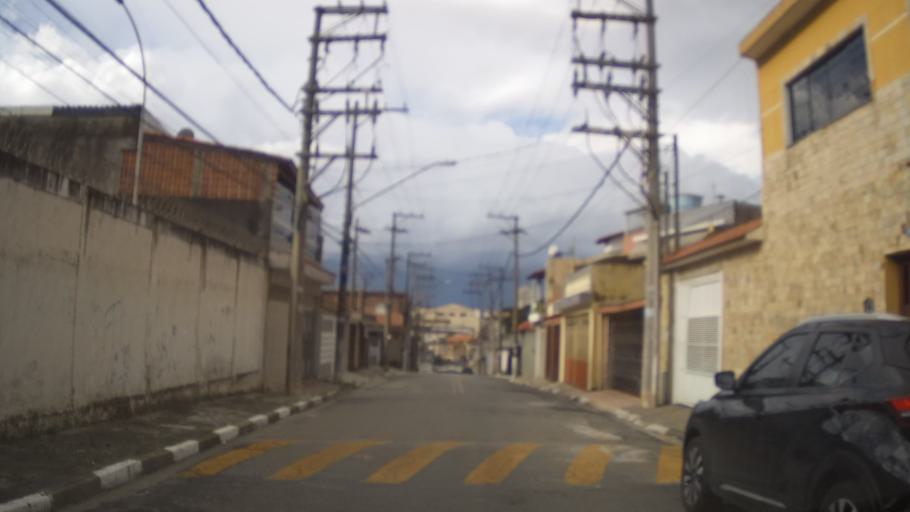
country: BR
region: Sao Paulo
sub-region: Guarulhos
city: Guarulhos
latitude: -23.4757
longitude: -46.5563
